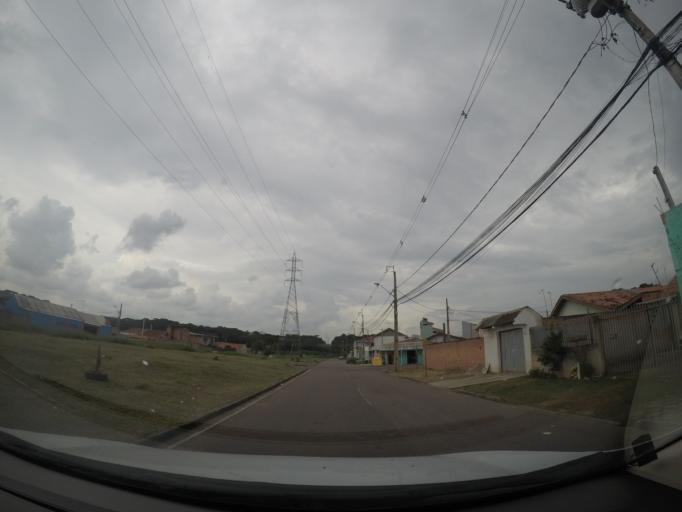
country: BR
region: Parana
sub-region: Sao Jose Dos Pinhais
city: Sao Jose dos Pinhais
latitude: -25.5557
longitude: -49.2458
